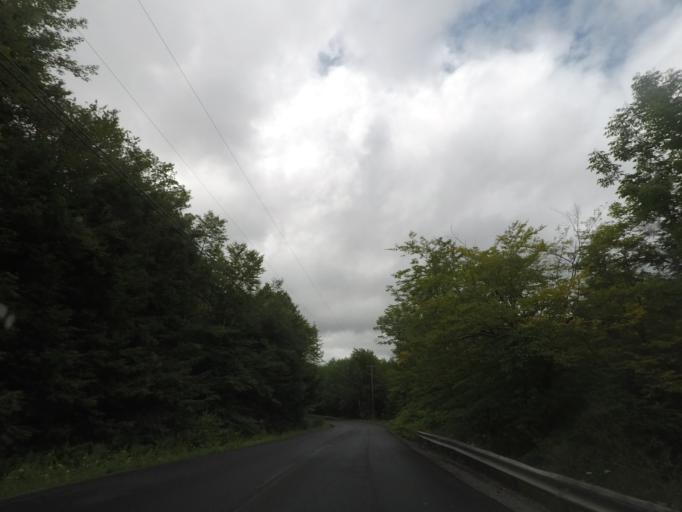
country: US
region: New York
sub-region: Rensselaer County
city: Poestenkill
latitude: 42.6904
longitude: -73.4673
